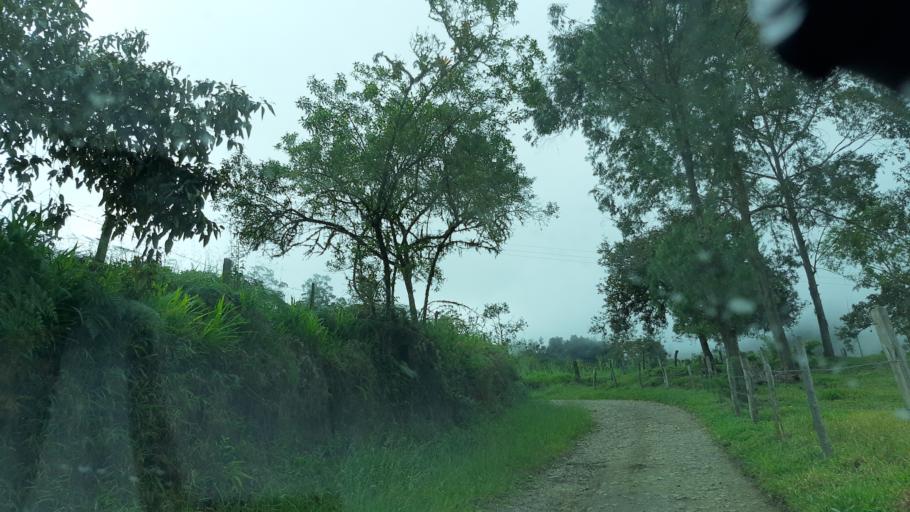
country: CO
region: Boyaca
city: Garagoa
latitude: 5.0431
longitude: -73.3472
